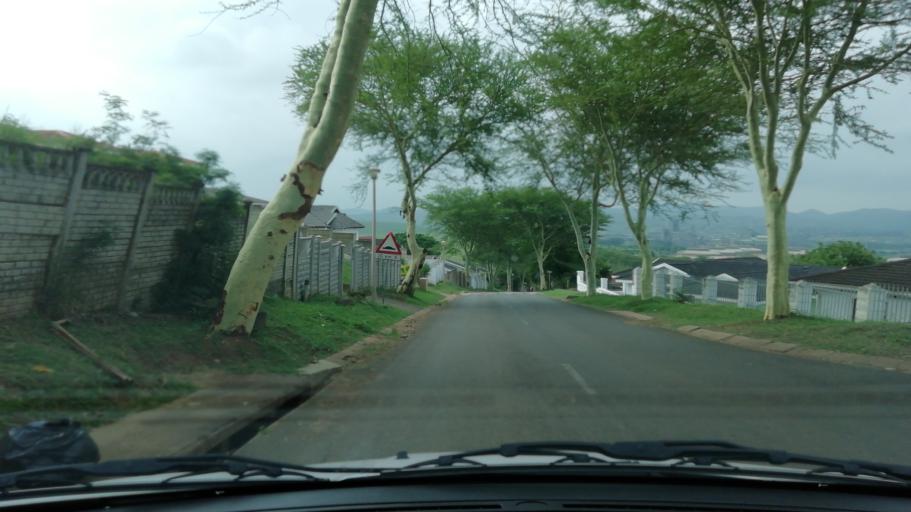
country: ZA
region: KwaZulu-Natal
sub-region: uThungulu District Municipality
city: Empangeni
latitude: -28.7388
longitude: 31.8782
